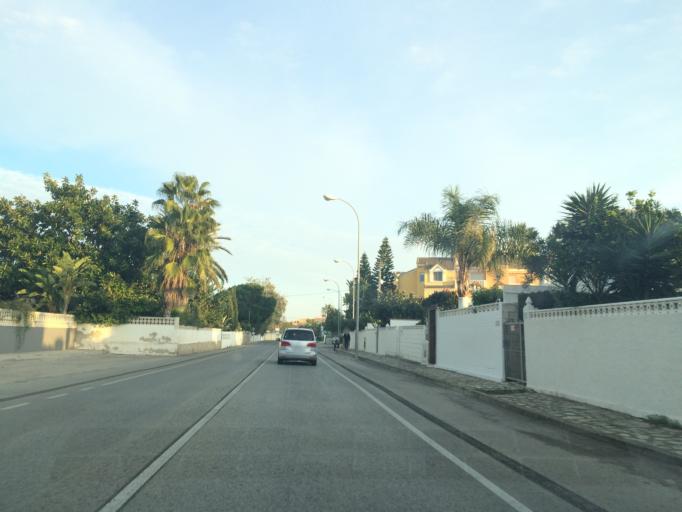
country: ES
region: Valencia
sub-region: Provincia de Alicante
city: Denia
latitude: 38.8547
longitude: 0.0831
